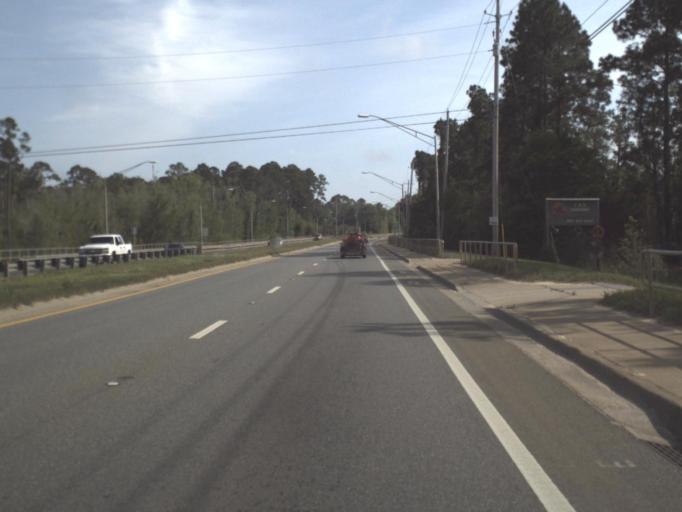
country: US
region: Florida
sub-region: Santa Rosa County
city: Navarre
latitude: 30.4404
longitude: -86.8663
